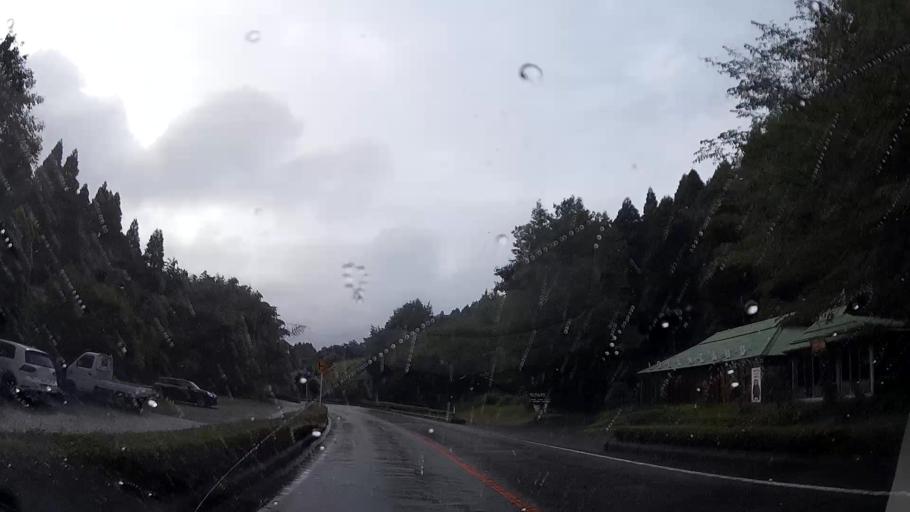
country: JP
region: Kumamoto
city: Aso
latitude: 32.8587
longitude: 131.0065
